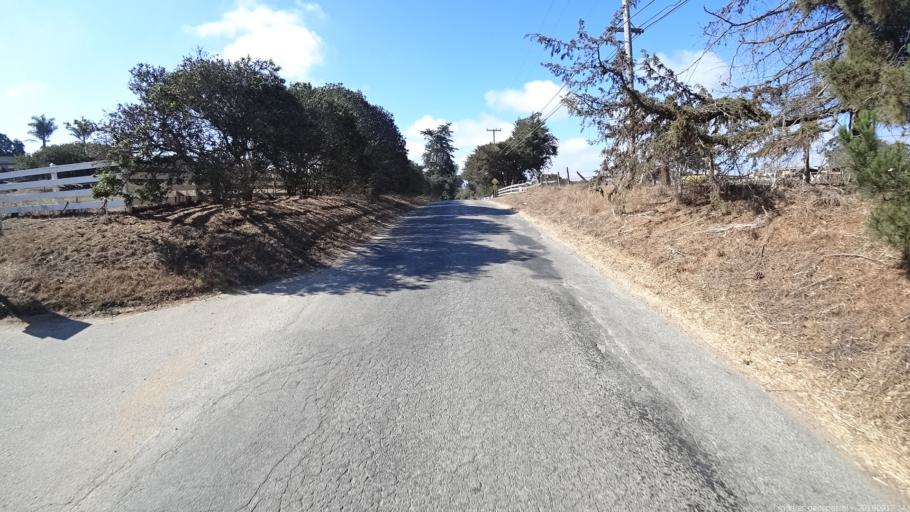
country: US
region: California
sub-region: Monterey County
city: Elkhorn
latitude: 36.7928
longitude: -121.7219
